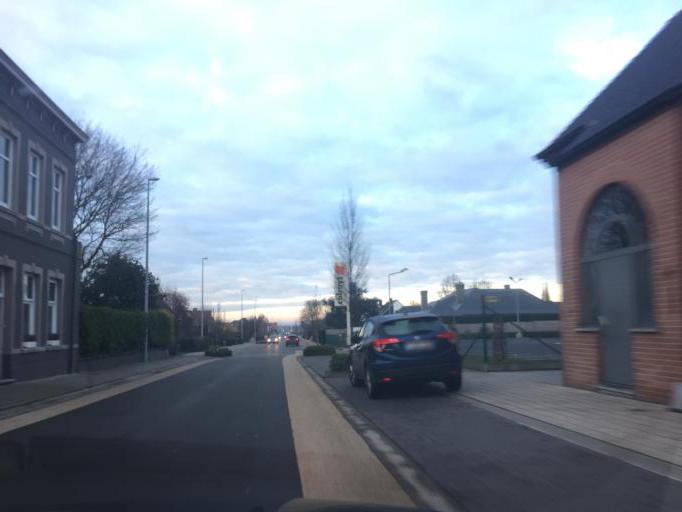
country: BE
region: Flanders
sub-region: Provincie West-Vlaanderen
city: Hooglede
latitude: 50.9755
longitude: 3.0780
